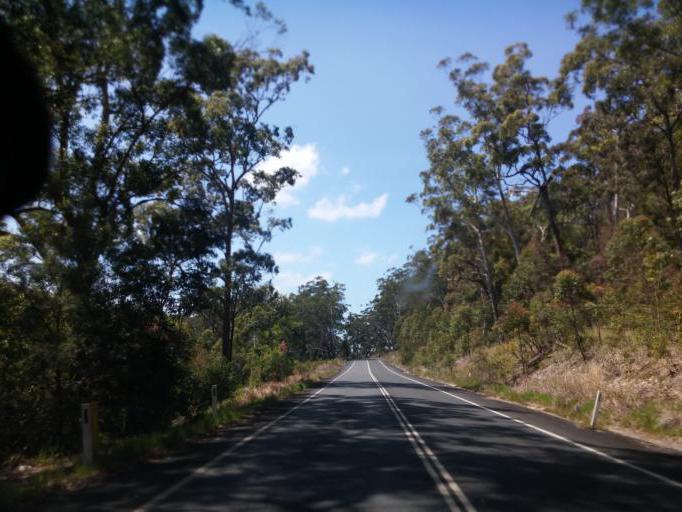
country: AU
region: New South Wales
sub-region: Great Lakes
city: Forster
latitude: -32.3800
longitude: 152.4514
